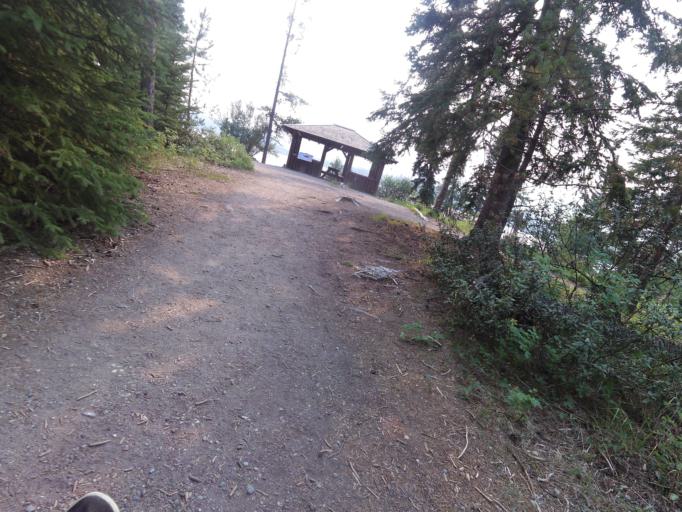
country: CA
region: Alberta
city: Jasper Park Lodge
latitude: 52.9249
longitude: -118.0978
